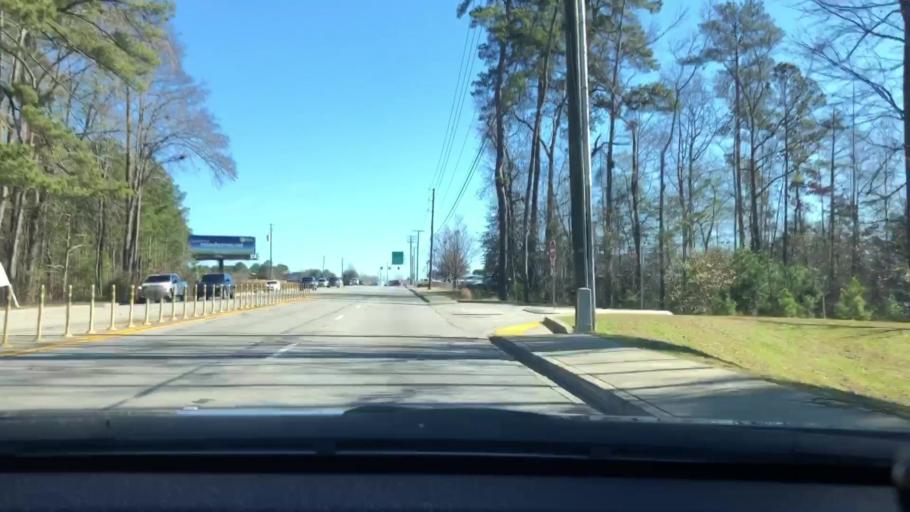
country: US
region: South Carolina
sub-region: Lexington County
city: Oak Grove
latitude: 34.0138
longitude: -81.1579
